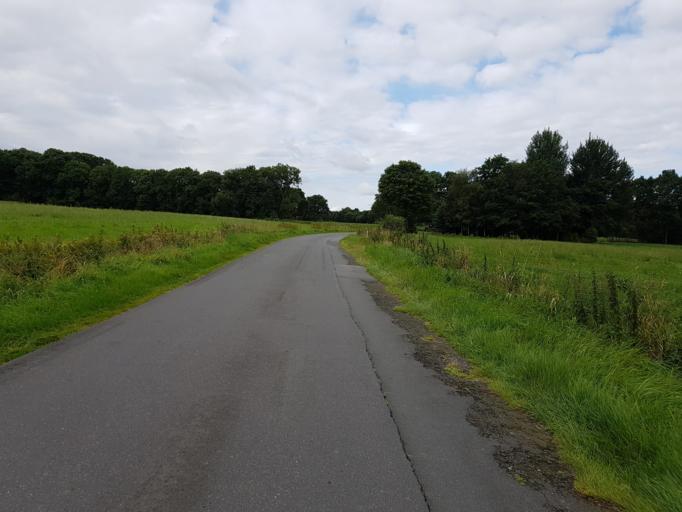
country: DE
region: Lower Saxony
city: Dunum
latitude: 53.5479
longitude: 7.6997
